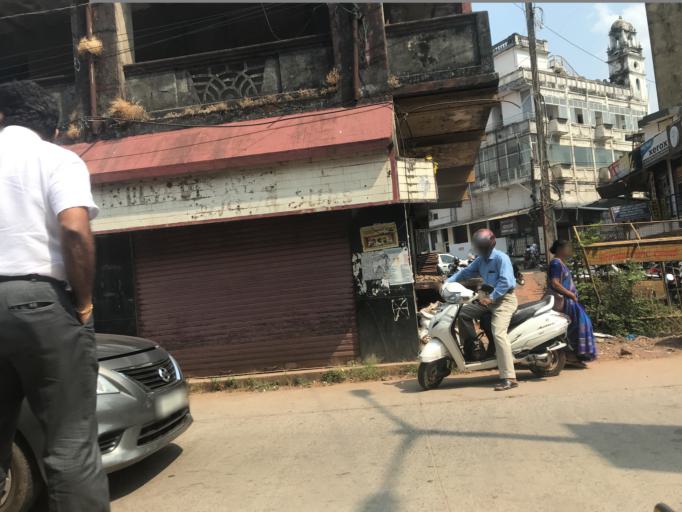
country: IN
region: Karnataka
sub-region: Dakshina Kannada
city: Mangalore
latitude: 12.8682
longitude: 74.8421
